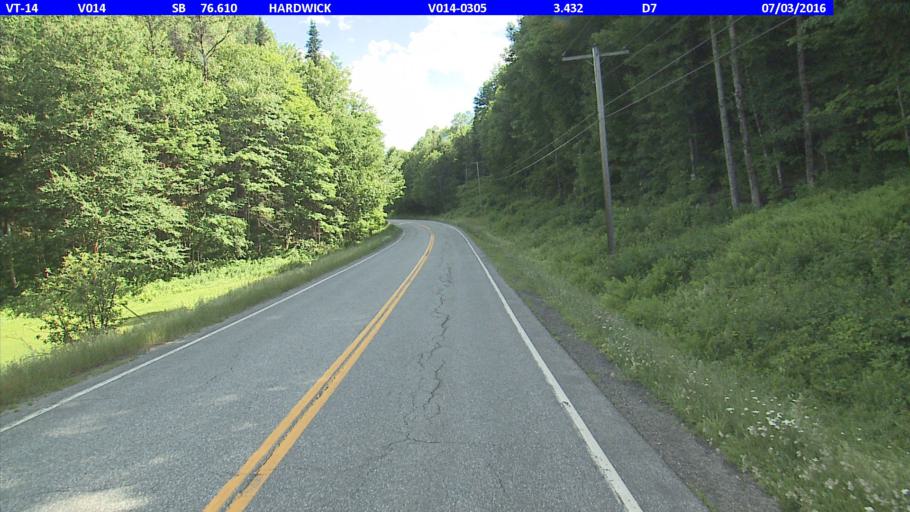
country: US
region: Vermont
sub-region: Caledonia County
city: Hardwick
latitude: 44.5436
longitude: -72.3738
